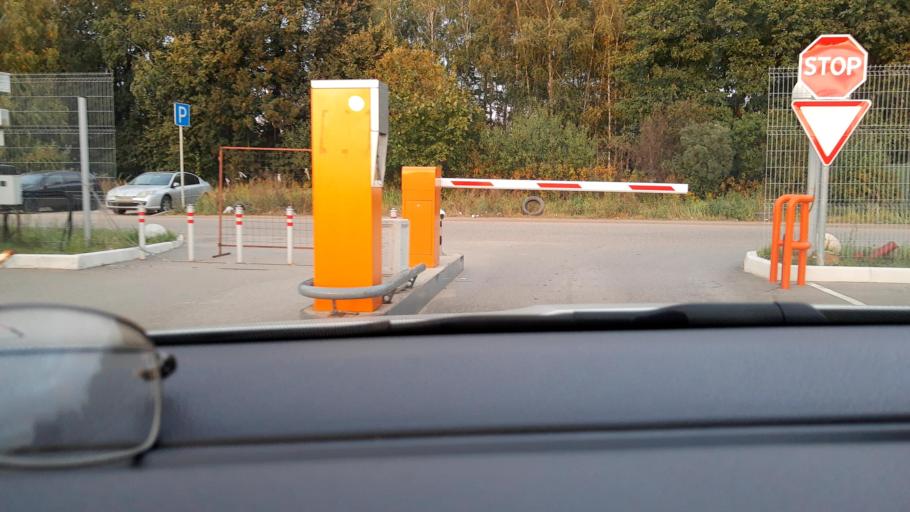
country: RU
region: Moskovskaya
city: Arkhangel'skoye
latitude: 55.8074
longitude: 37.2985
